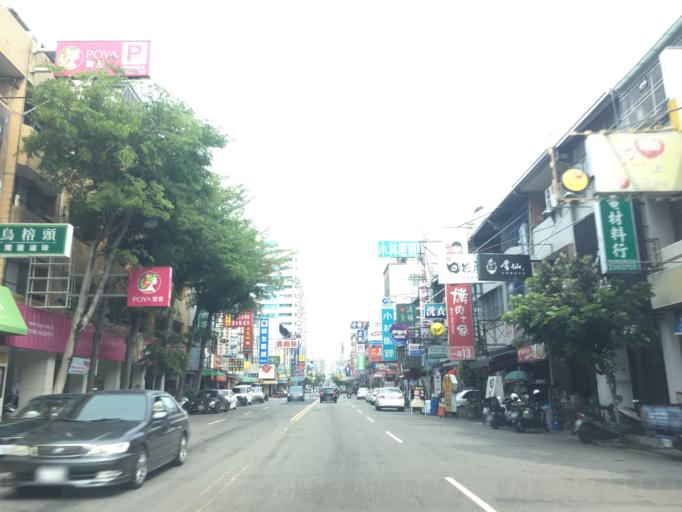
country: TW
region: Taiwan
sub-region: Taichung City
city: Taichung
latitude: 24.1671
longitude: 120.6808
